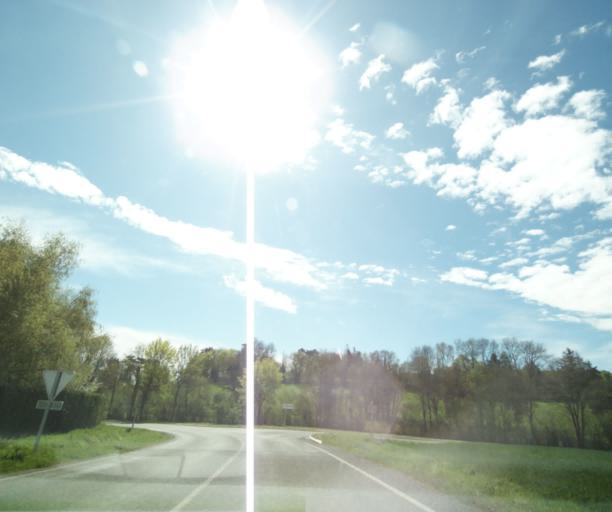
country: FR
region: Bourgogne
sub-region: Departement de Saone-et-Loire
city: Charnay-les-Macon
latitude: 46.2977
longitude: 4.7647
